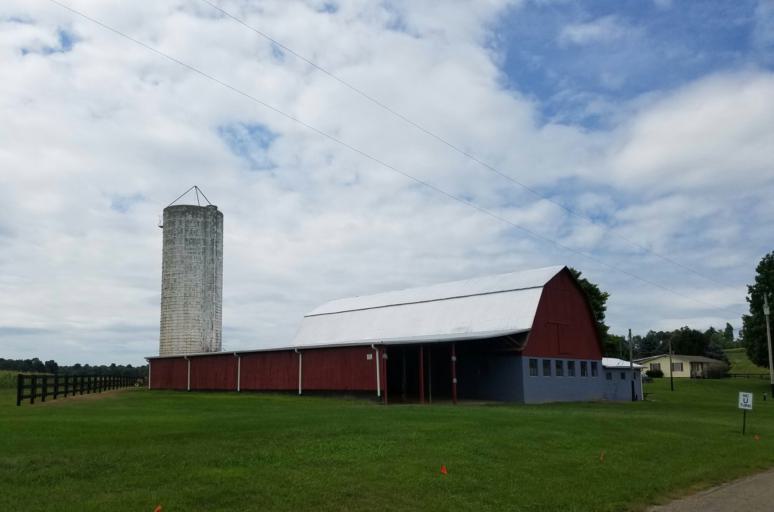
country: US
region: Ohio
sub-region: Sandusky County
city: Bellville
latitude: 40.5491
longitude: -82.4140
